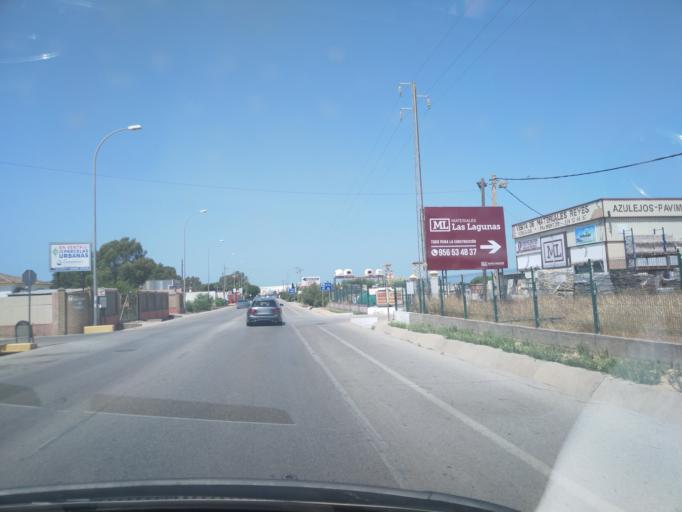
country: ES
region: Andalusia
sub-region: Provincia de Cadiz
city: Chiclana de la Frontera
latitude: 36.3955
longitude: -6.1610
